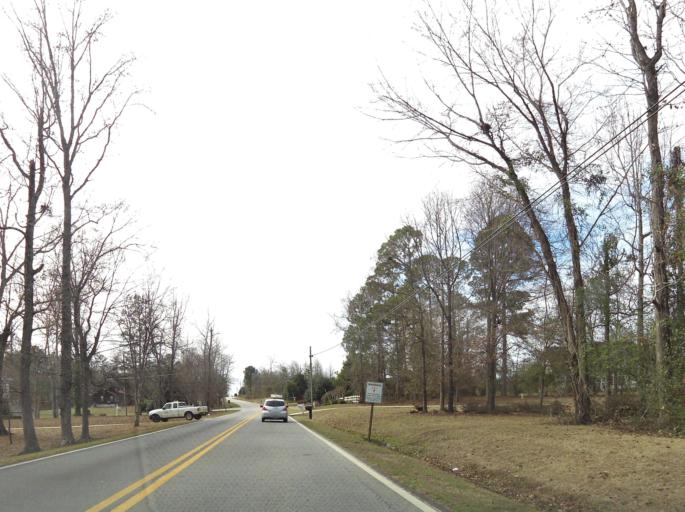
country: US
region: Georgia
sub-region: Bibb County
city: West Point
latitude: 32.8086
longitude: -83.7803
